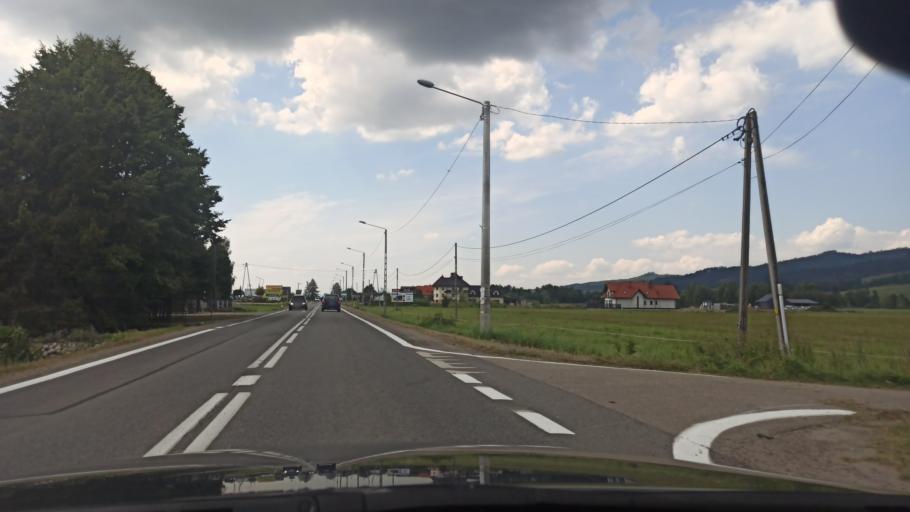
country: PL
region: Lesser Poland Voivodeship
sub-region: Powiat nowotarski
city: Lopuszna
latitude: 49.4719
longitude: 20.1221
